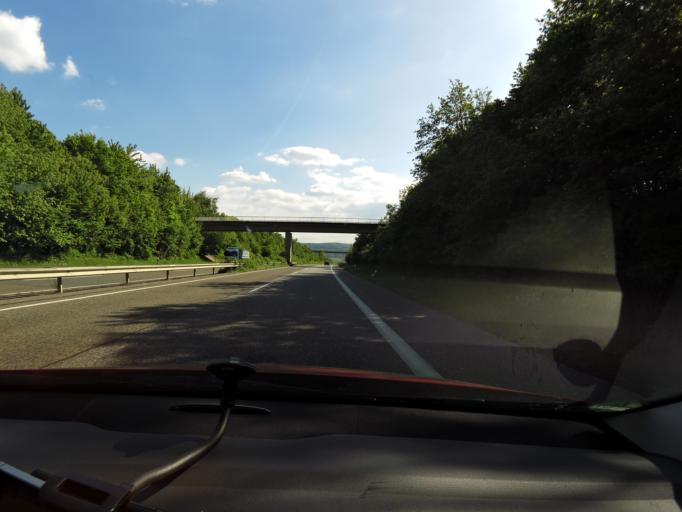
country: DE
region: Rheinland-Pfalz
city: Bad Neuenahr-Ahrweiler
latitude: 50.5653
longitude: 7.1190
